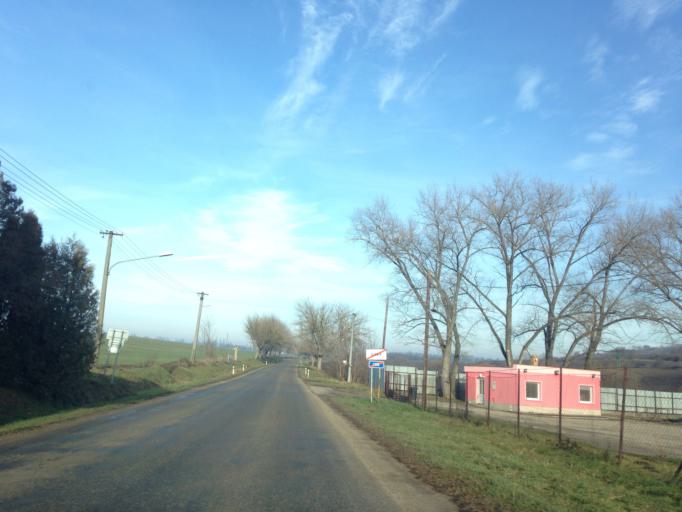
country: SK
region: Nitriansky
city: Svodin
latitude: 47.9656
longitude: 18.4099
